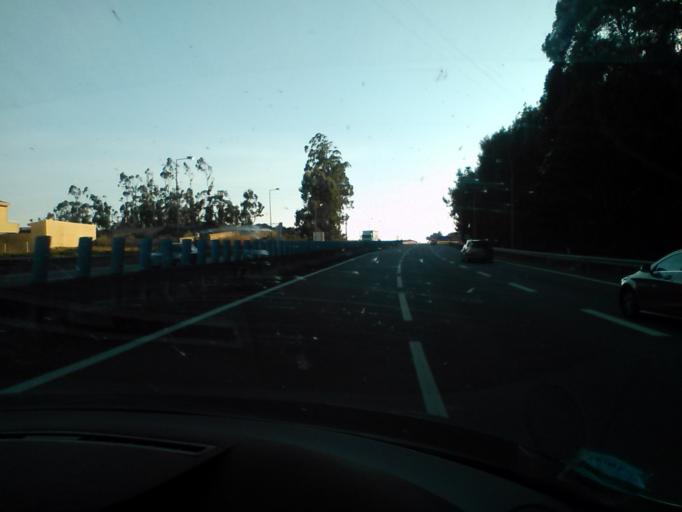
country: PT
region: Porto
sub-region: Vila do Conde
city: Vila do Conde
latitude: 41.3767
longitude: -8.7212
